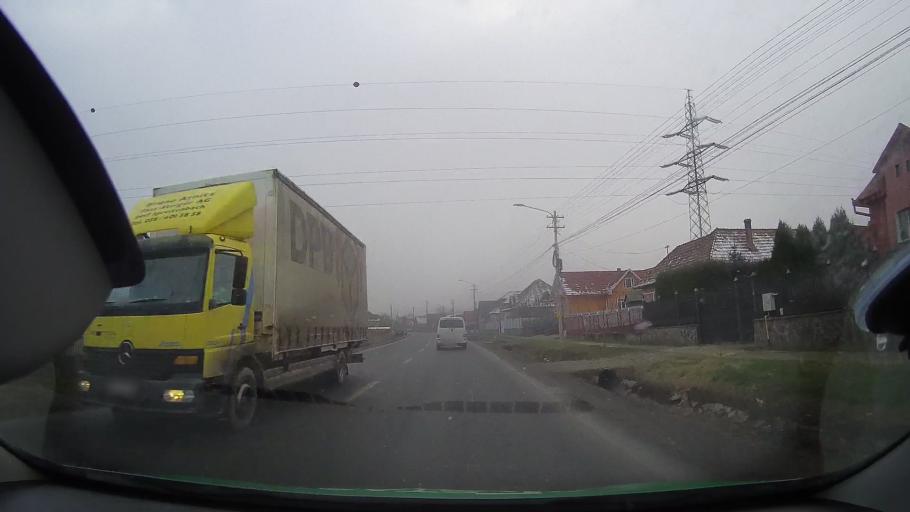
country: RO
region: Mures
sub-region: Municipiul Tarnaveni
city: Tarnaveni
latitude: 46.3136
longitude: 24.2975
